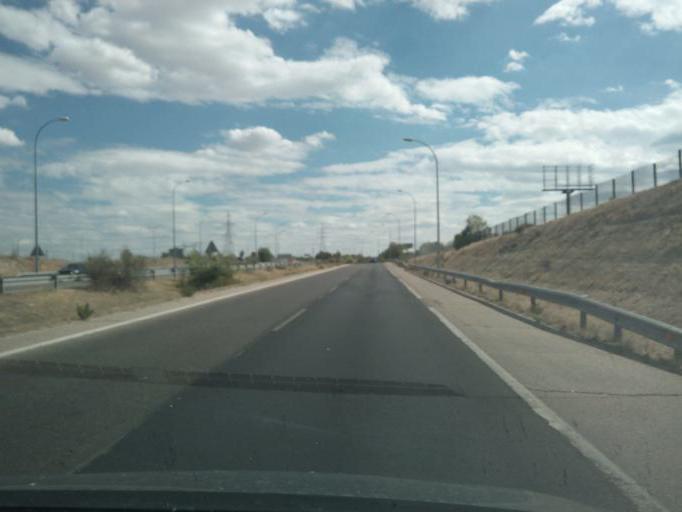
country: ES
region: Madrid
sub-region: Provincia de Madrid
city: San Sebastian de los Reyes
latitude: 40.5568
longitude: -3.6085
